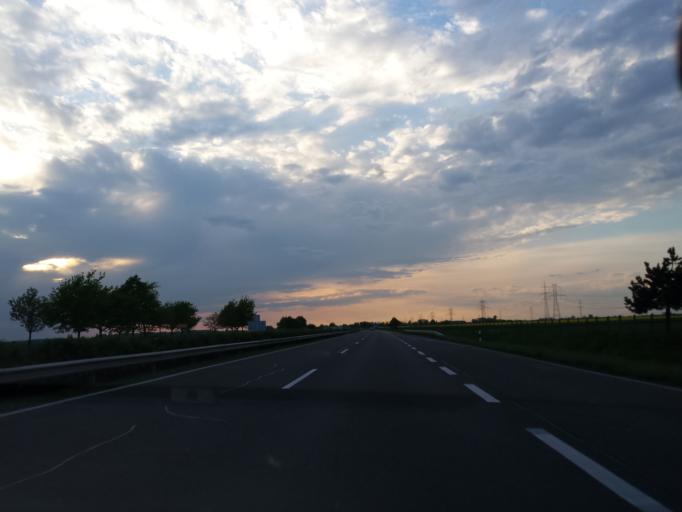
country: HU
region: Gyor-Moson-Sopron
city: Lebeny
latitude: 47.7534
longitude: 17.4120
